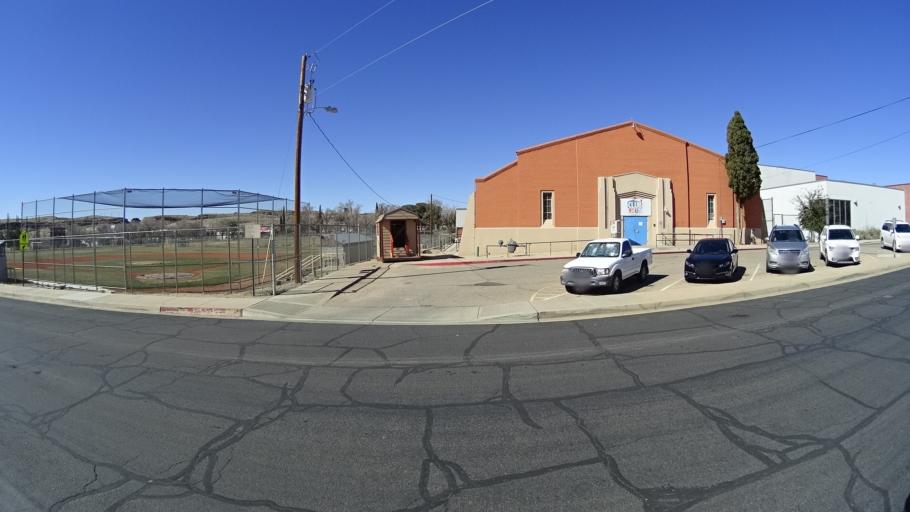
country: US
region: Arizona
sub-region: Mohave County
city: Kingman
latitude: 35.1914
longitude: -114.0578
